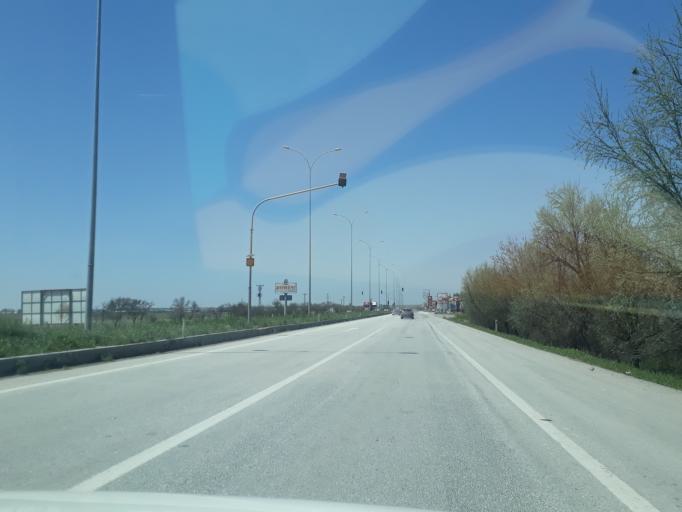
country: TR
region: Konya
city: Karapinar
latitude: 37.7146
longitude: 33.5177
